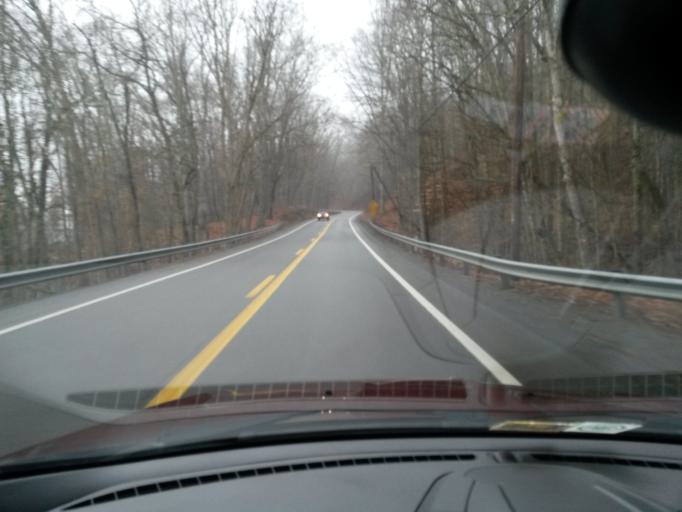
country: US
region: West Virginia
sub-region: Greenbrier County
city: Lewisburg
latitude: 37.8735
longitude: -80.5330
